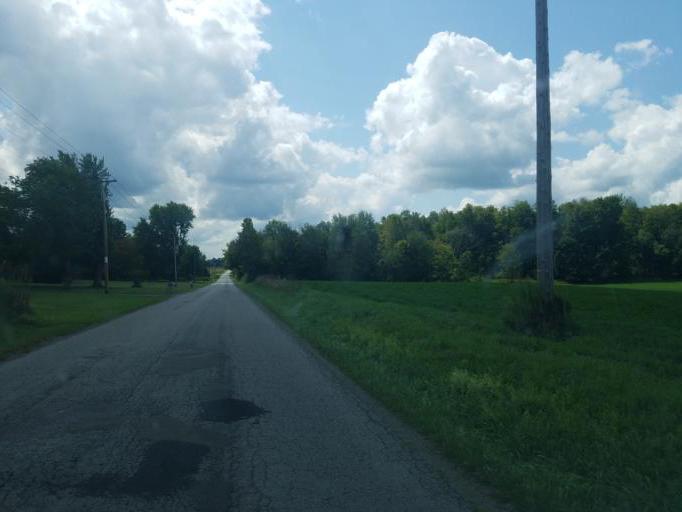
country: US
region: Ohio
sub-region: Morrow County
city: Mount Gilead
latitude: 40.5262
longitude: -82.7415
